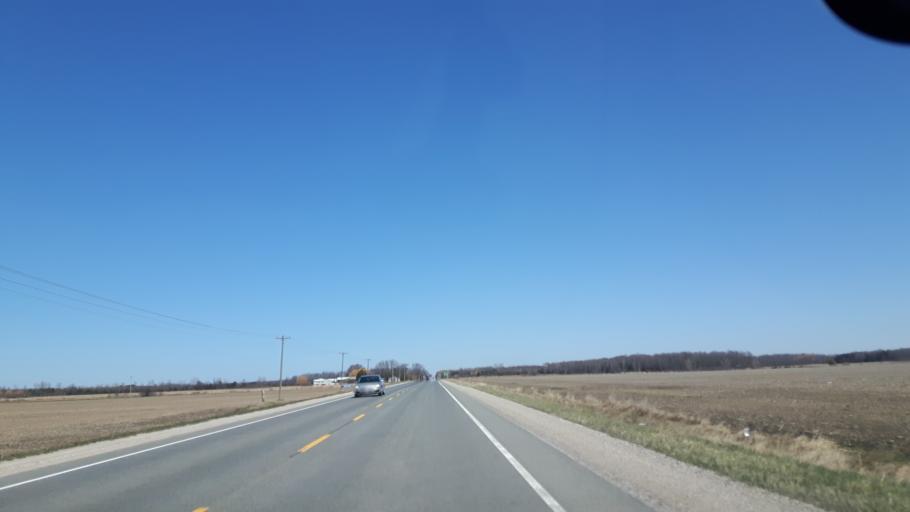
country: CA
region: Ontario
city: Goderich
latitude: 43.6361
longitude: -81.7057
